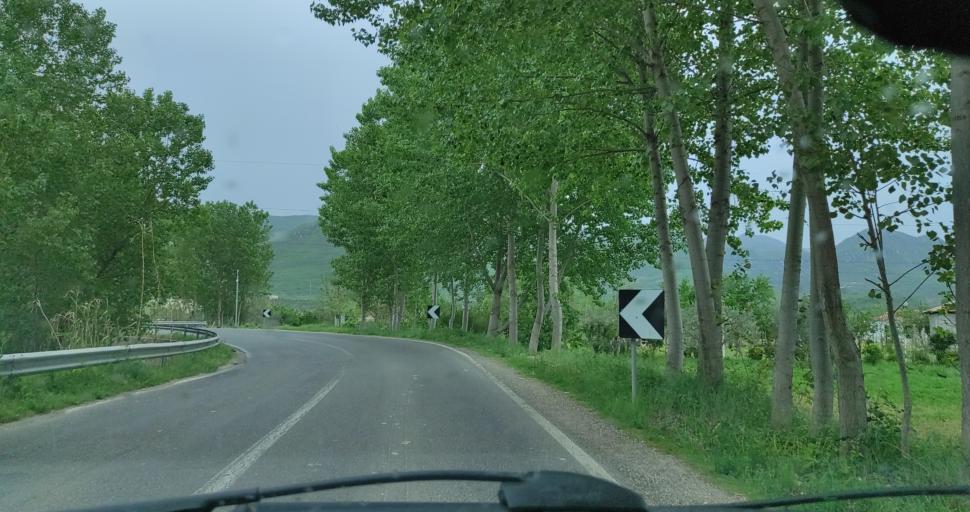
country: AL
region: Lezhe
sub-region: Rrethi i Kurbinit
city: Mamurras
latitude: 41.6019
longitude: 19.7051
